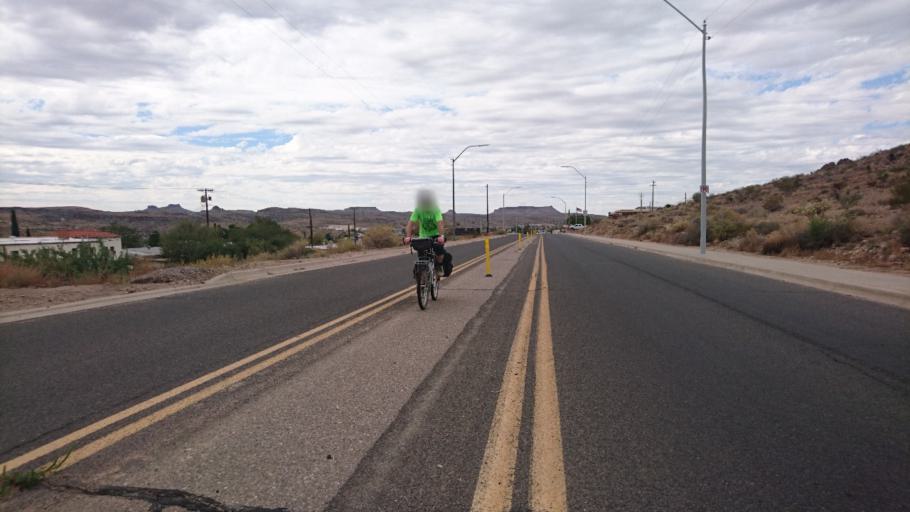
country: US
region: Arizona
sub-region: Mohave County
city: Kingman
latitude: 35.1874
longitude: -114.0424
